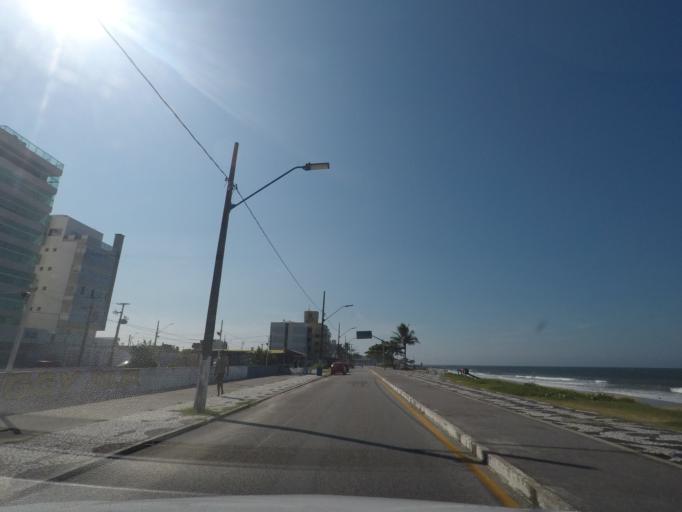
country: BR
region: Parana
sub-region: Guaratuba
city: Guaratuba
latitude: -25.8217
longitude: -48.5317
